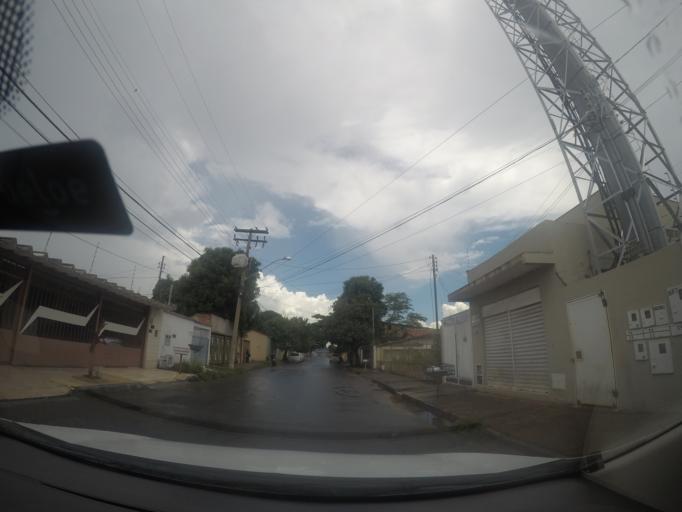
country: BR
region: Goias
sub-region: Goiania
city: Goiania
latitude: -16.6811
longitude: -49.2882
